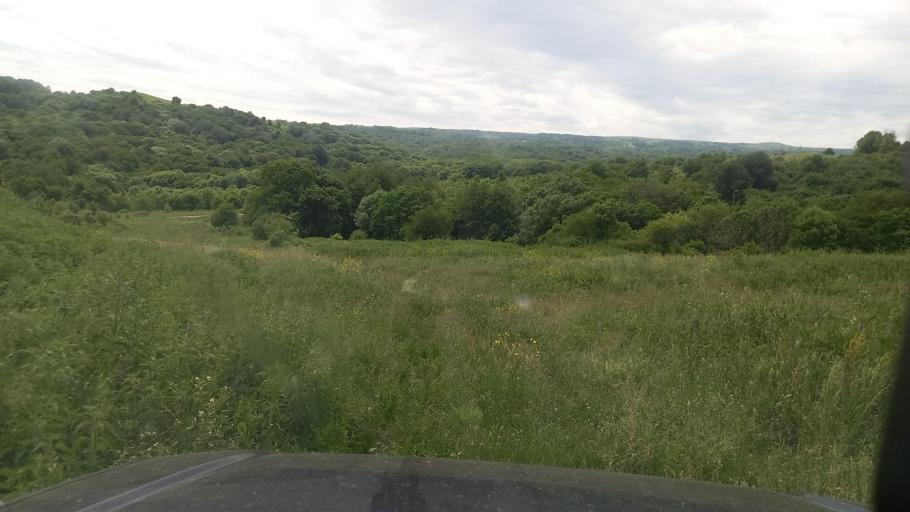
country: RU
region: Karachayevo-Cherkesiya
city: Pregradnaya
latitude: 44.0959
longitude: 41.1664
